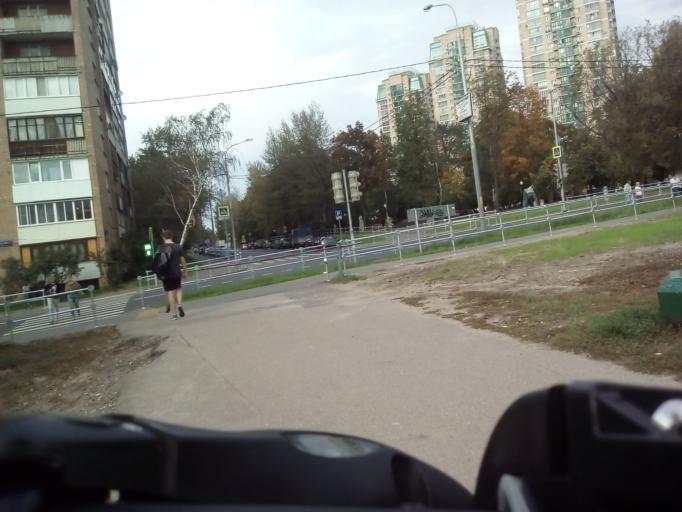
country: RU
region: Moscow
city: Rostokino
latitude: 55.8320
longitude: 37.6586
